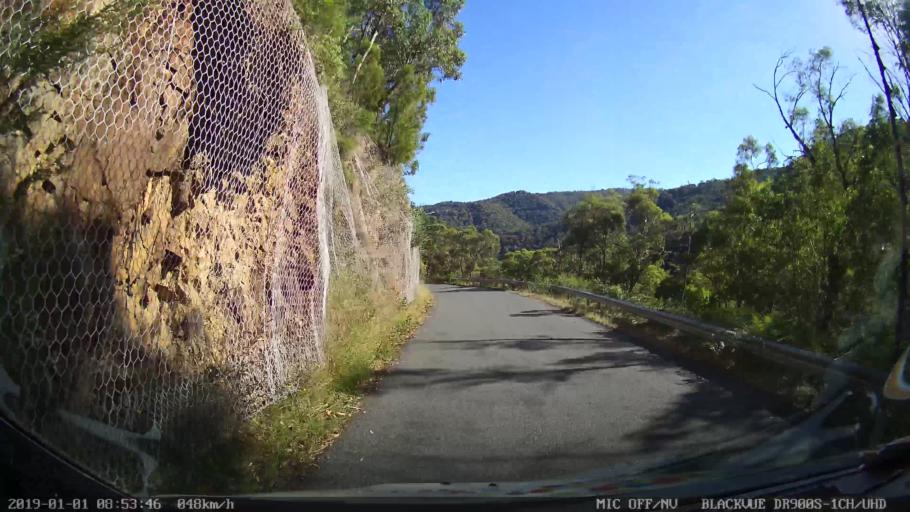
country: AU
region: New South Wales
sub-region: Snowy River
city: Jindabyne
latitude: -36.2637
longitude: 148.1898
